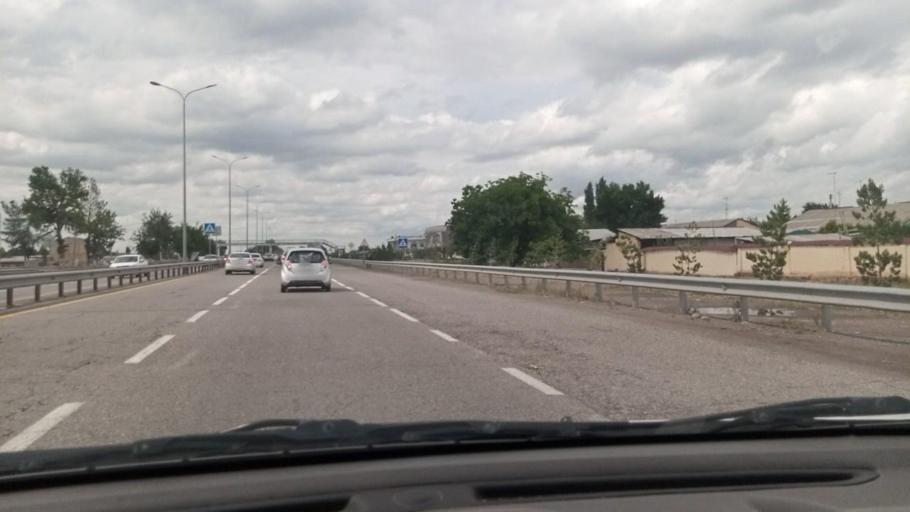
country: UZ
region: Toshkent
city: Tuytepa
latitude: 41.1279
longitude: 69.4373
